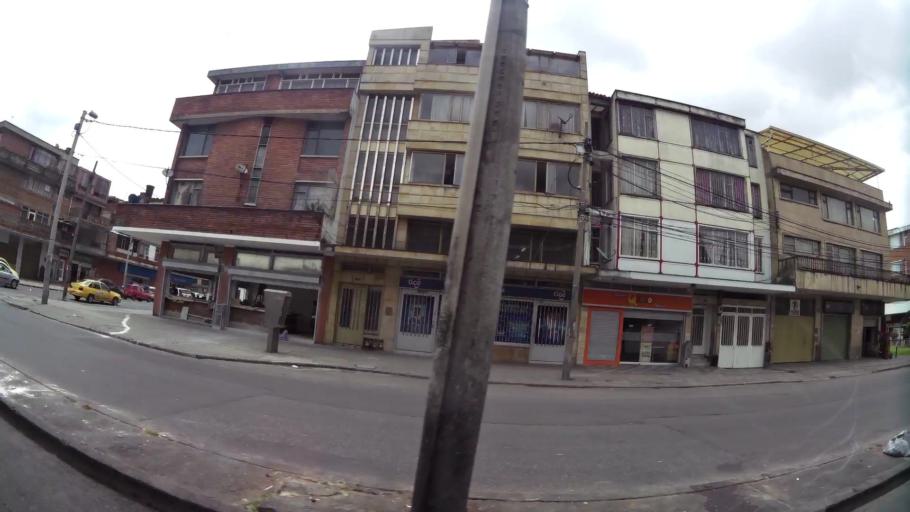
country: CO
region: Bogota D.C.
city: Bogota
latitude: 4.5980
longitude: -74.1004
